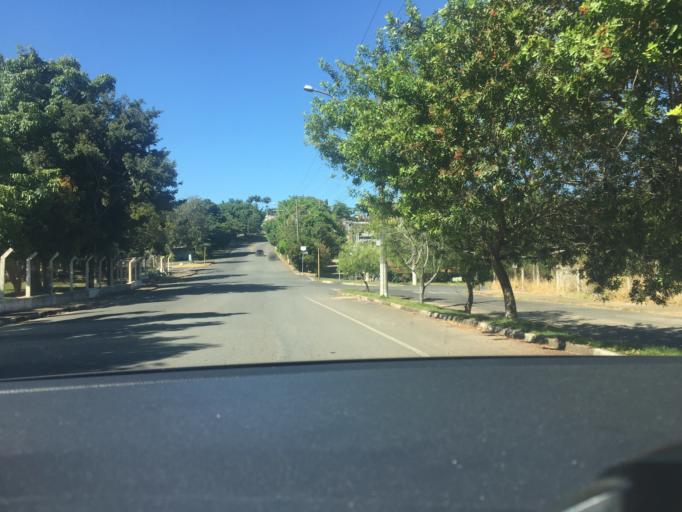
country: BR
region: Sao Paulo
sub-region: Santo Antonio Do Jardim
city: Espirito Santo do Pinhal
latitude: -22.1796
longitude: -46.7449
